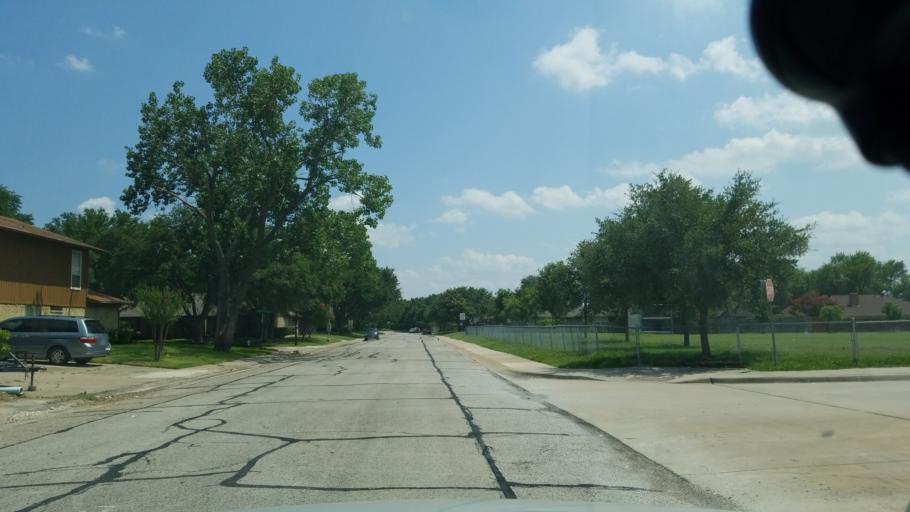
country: US
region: Texas
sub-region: Dallas County
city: Carrollton
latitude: 32.9664
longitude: -96.8627
